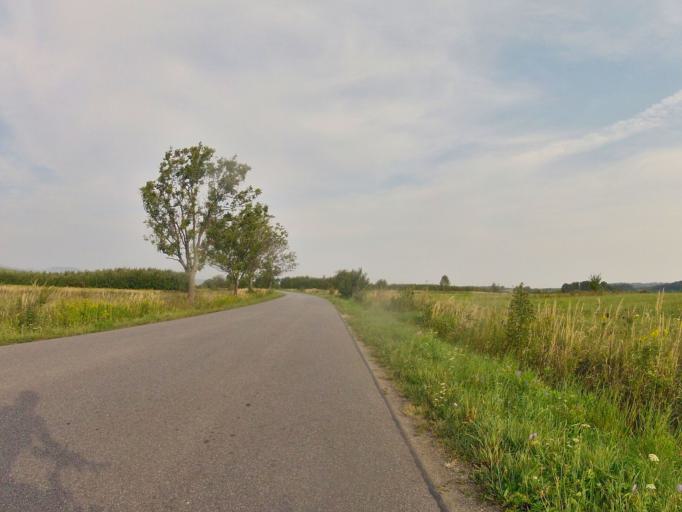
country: PL
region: Subcarpathian Voivodeship
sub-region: Powiat jasielski
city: Nowy Zmigrod
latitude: 49.6228
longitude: 21.5134
